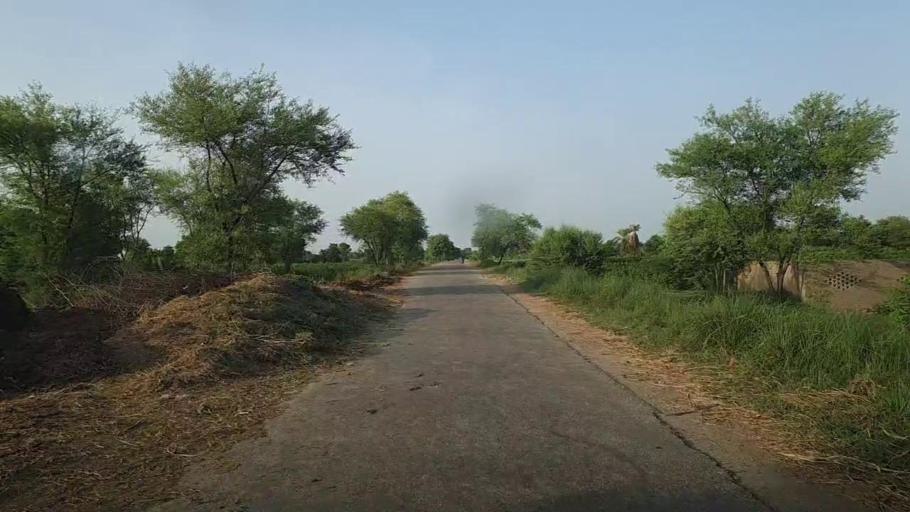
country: PK
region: Sindh
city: Ubauro
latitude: 28.1268
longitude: 69.8304
